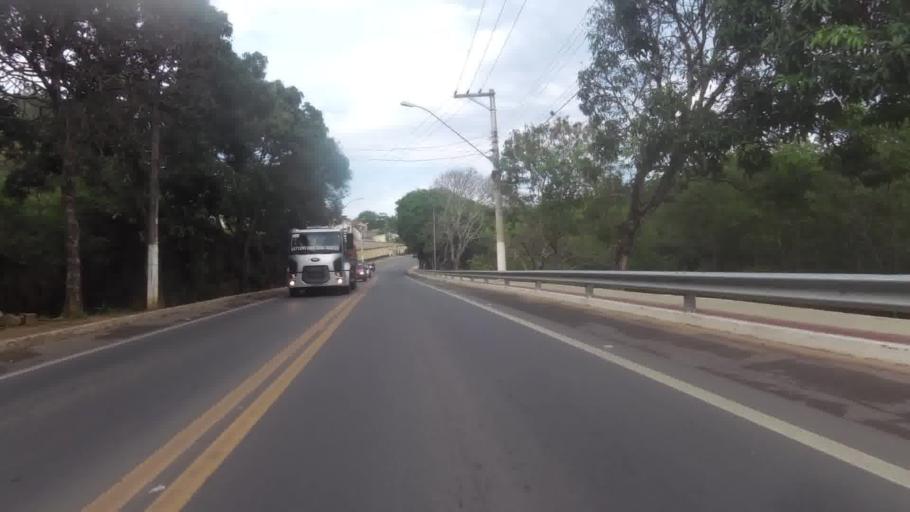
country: BR
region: Espirito Santo
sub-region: Piuma
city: Piuma
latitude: -20.8070
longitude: -40.6572
